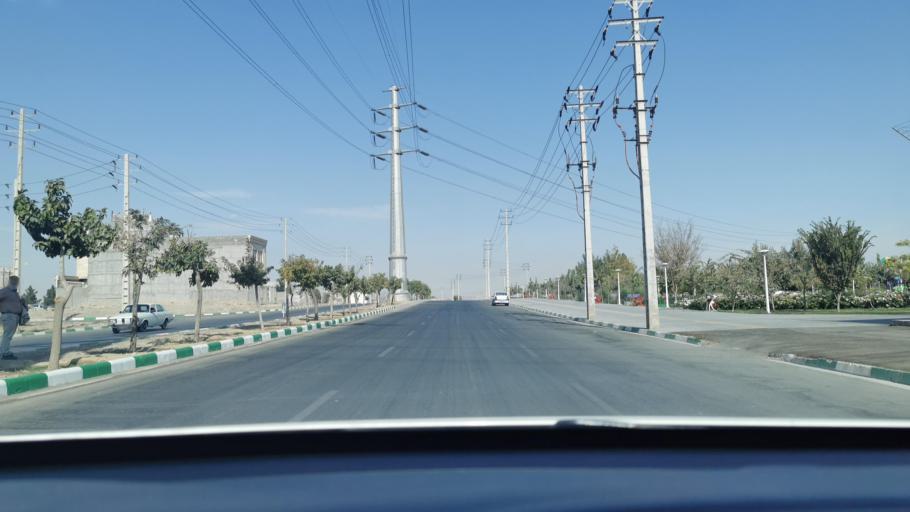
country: IR
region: Razavi Khorasan
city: Mashhad
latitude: 36.3421
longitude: 59.6094
